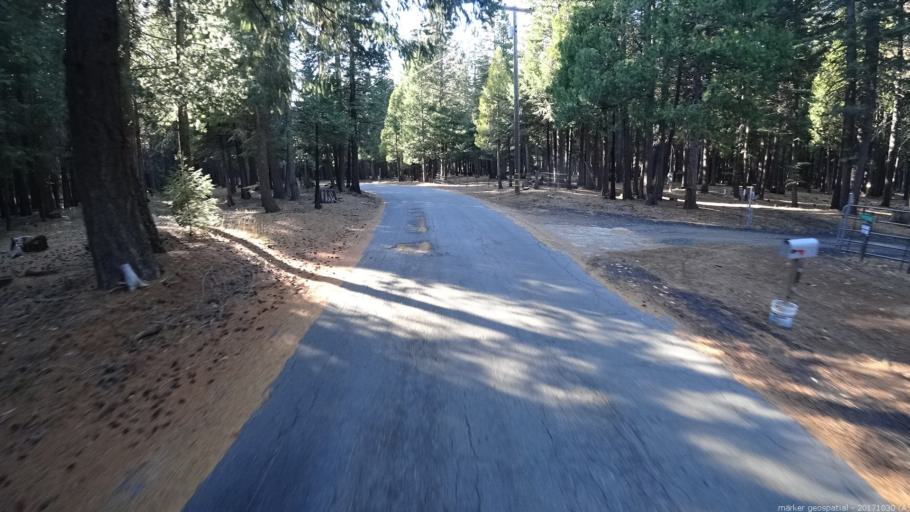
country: US
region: California
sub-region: Shasta County
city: Shingletown
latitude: 40.5597
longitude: -121.7244
